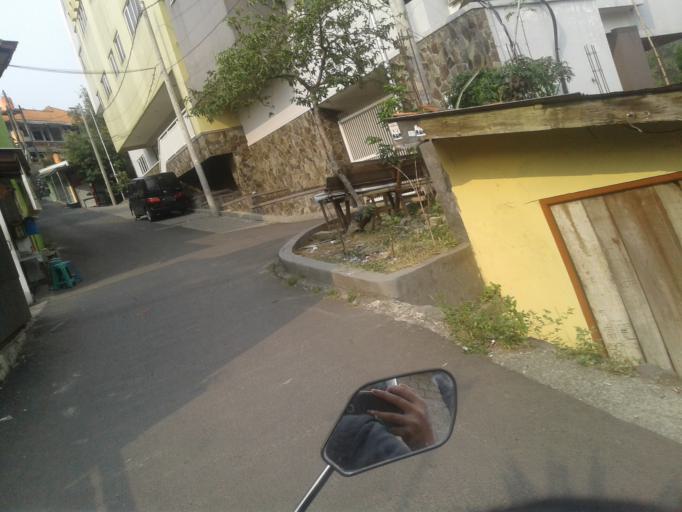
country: ID
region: West Java
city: Depok
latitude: -6.3694
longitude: 106.8366
